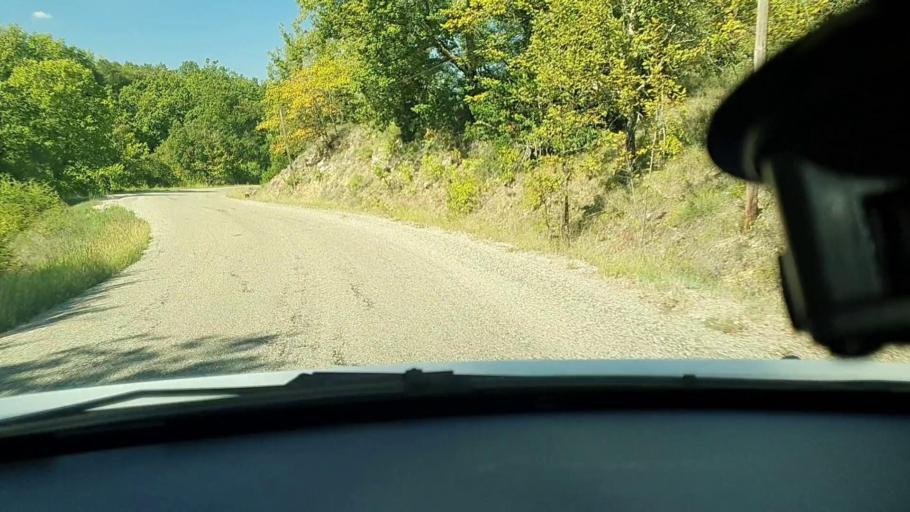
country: FR
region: Languedoc-Roussillon
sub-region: Departement du Gard
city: Goudargues
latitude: 44.1670
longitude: 4.3909
